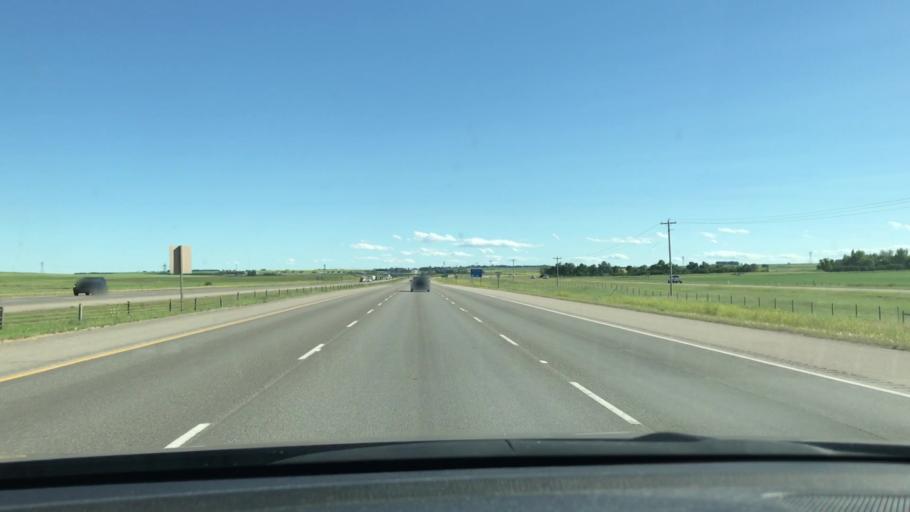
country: CA
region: Alberta
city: Crossfield
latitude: 51.4864
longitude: -114.0254
